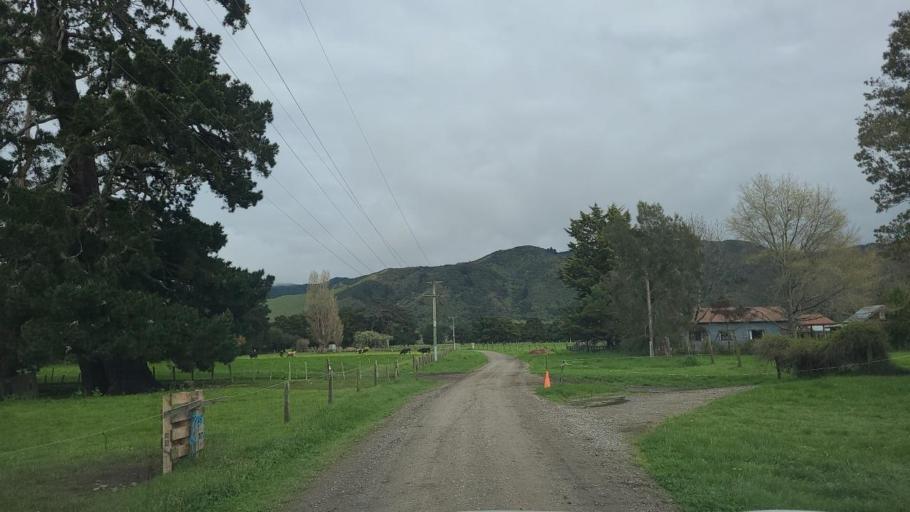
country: NZ
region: Wellington
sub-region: Masterton District
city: Masterton
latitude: -41.0562
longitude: 175.4102
